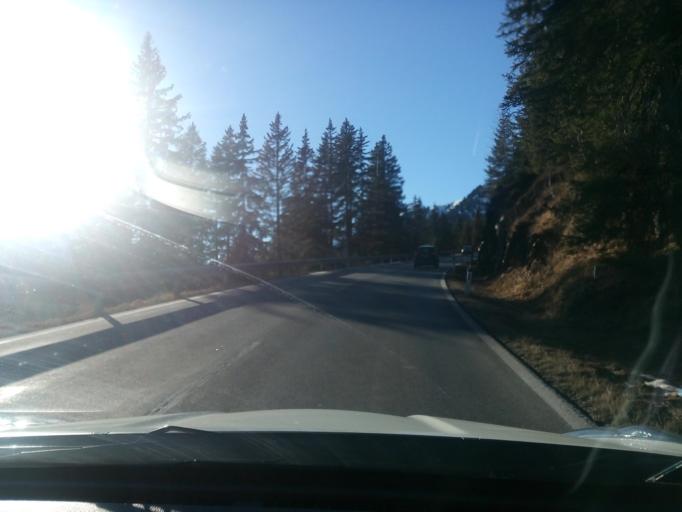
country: AT
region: Tyrol
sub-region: Politischer Bezirk Landeck
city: Sankt Anton am Arlberg
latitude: 47.1198
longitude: 10.2356
